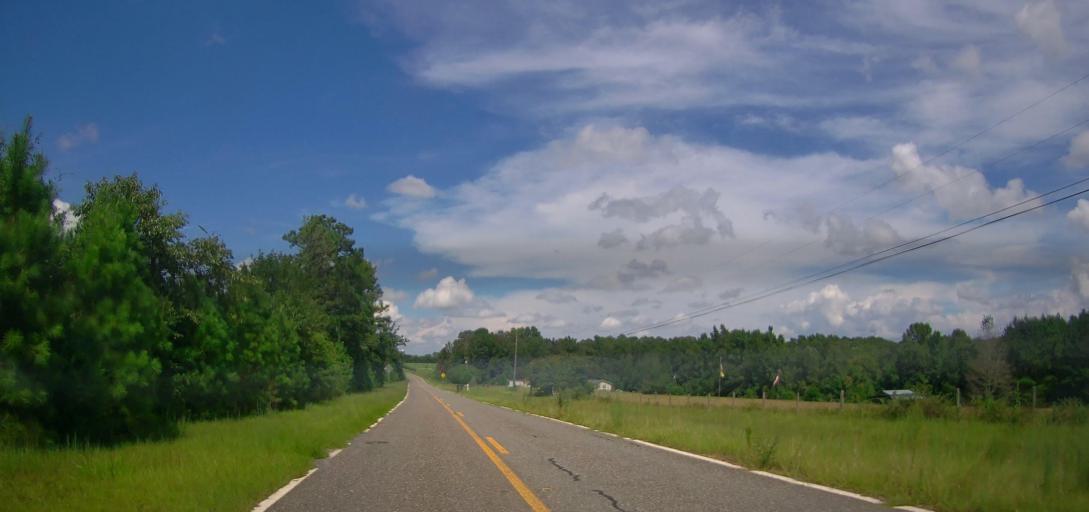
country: US
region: Georgia
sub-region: Peach County
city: Fort Valley
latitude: 32.5223
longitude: -83.8270
